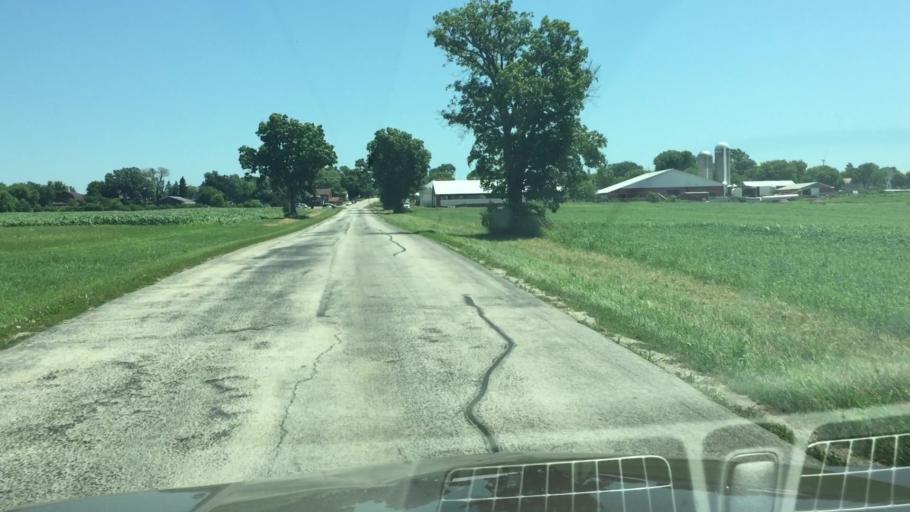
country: US
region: Wisconsin
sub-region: Fond du Lac County
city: Saint Peter
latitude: 43.9365
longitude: -88.3096
